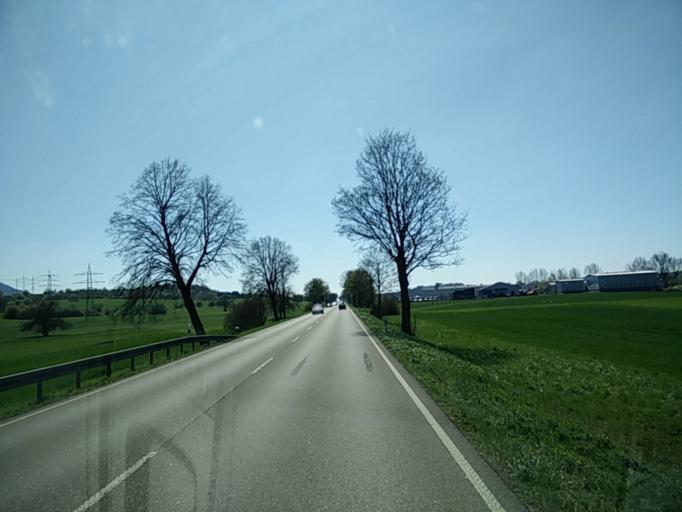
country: DE
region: Baden-Wuerttemberg
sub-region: Tuebingen Region
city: Nehren
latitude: 48.4310
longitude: 9.0509
